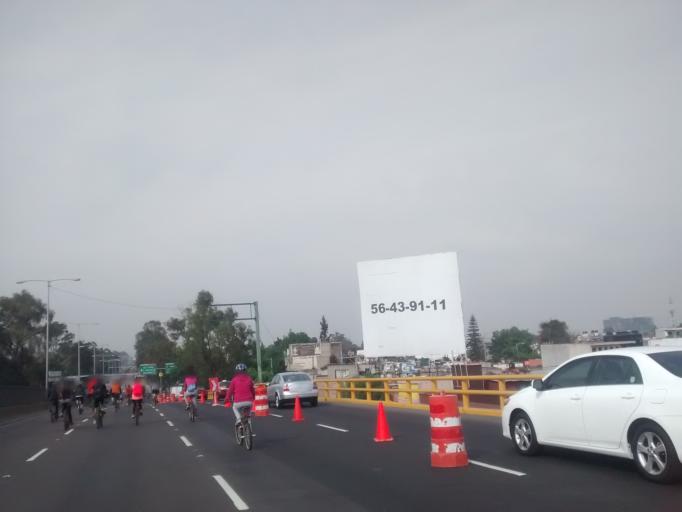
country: MX
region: Mexico City
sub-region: Iztacalco
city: Iztacalco
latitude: 19.3702
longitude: -99.1085
